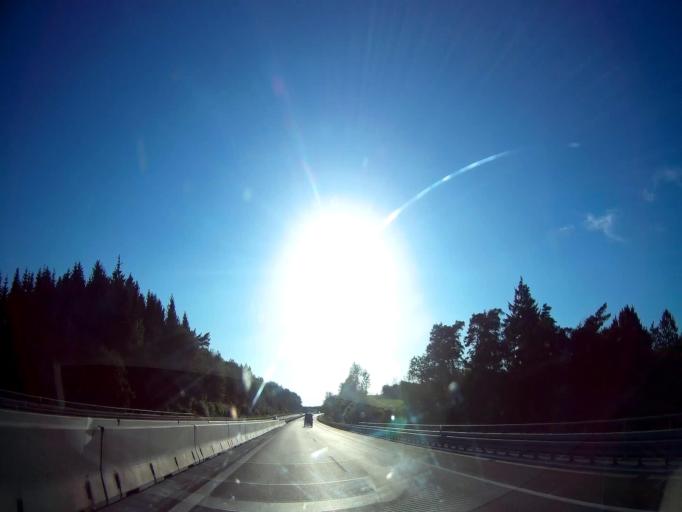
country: DE
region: Bavaria
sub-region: Upper Palatinate
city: Parsberg
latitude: 49.1808
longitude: 11.7046
